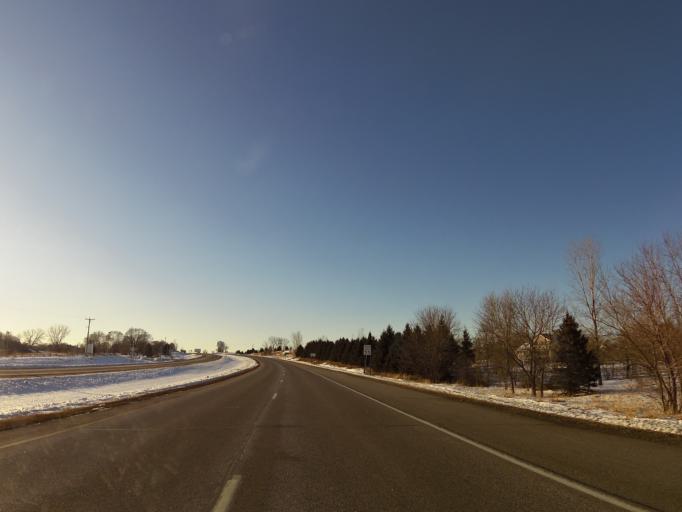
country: US
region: Minnesota
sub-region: Washington County
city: Lake Elmo
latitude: 44.9974
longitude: -92.9253
